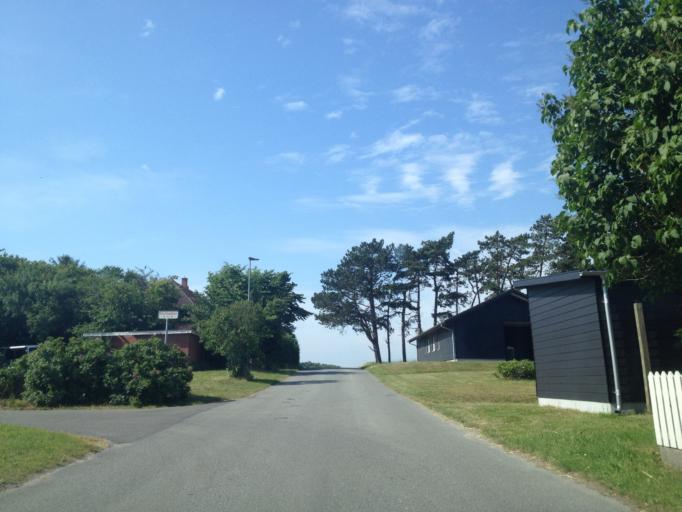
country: DK
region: Central Jutland
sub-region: Samso Kommune
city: Tranebjerg
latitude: 55.8015
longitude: 10.5577
